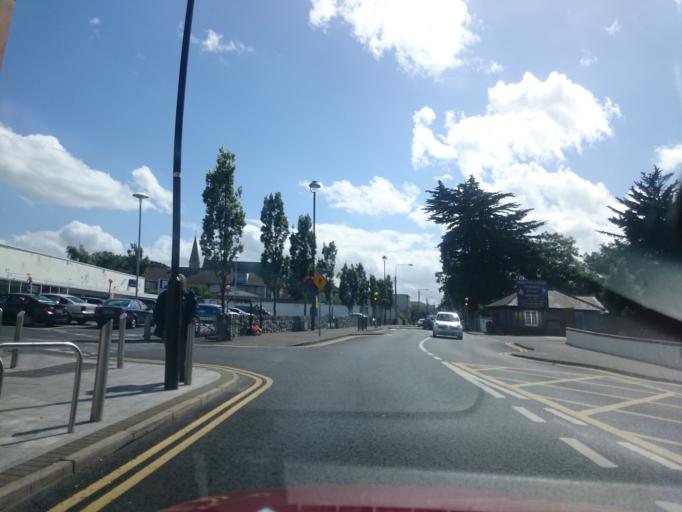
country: IE
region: Leinster
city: Clondalkin
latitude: 53.3203
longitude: -6.3946
